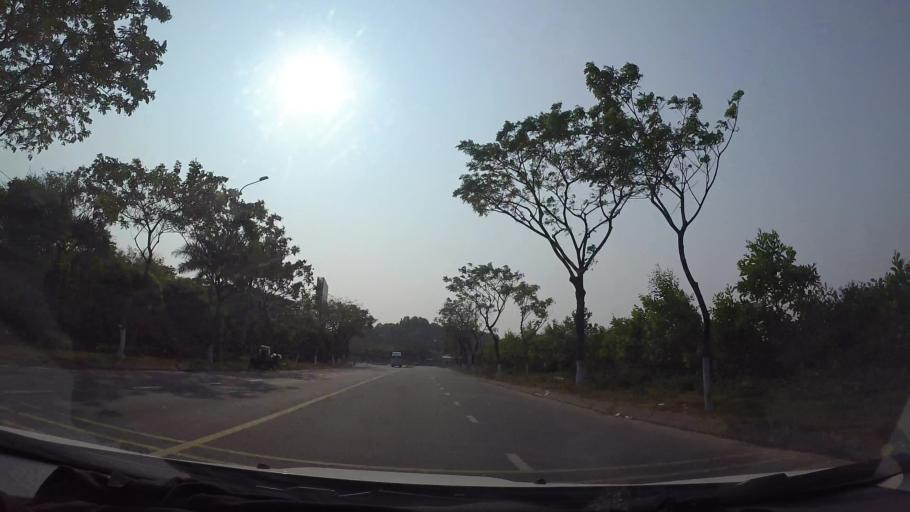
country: VN
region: Da Nang
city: Cam Le
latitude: 16.0151
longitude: 108.1945
